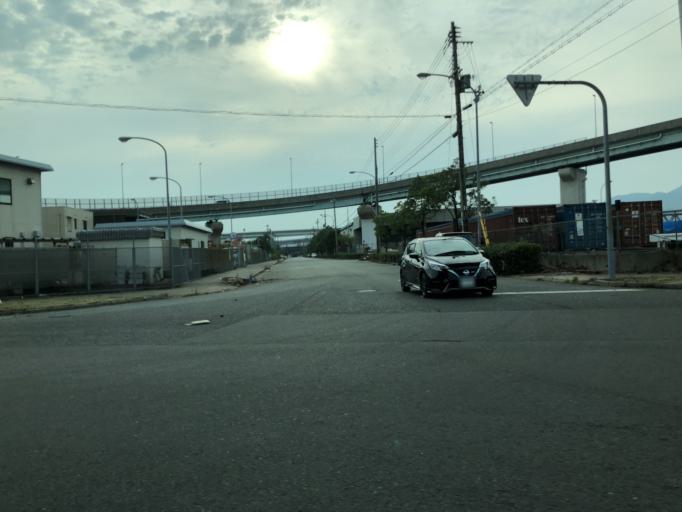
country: JP
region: Hyogo
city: Ashiya
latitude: 34.6959
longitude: 135.2734
